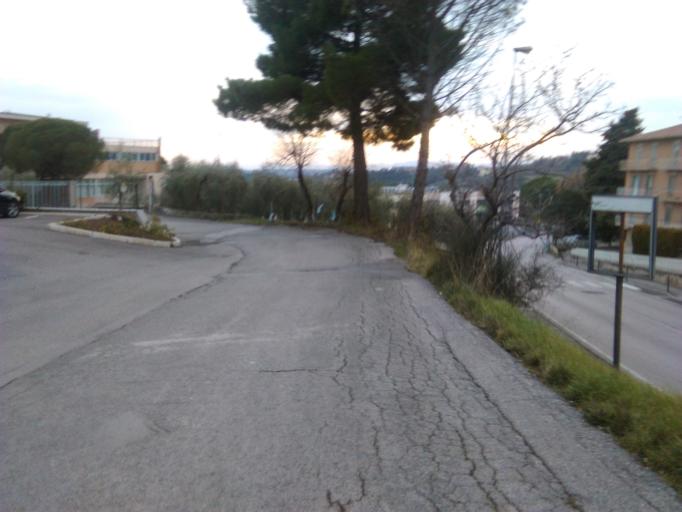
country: IT
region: Umbria
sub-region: Provincia di Perugia
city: Perugia
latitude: 43.0963
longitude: 12.3635
